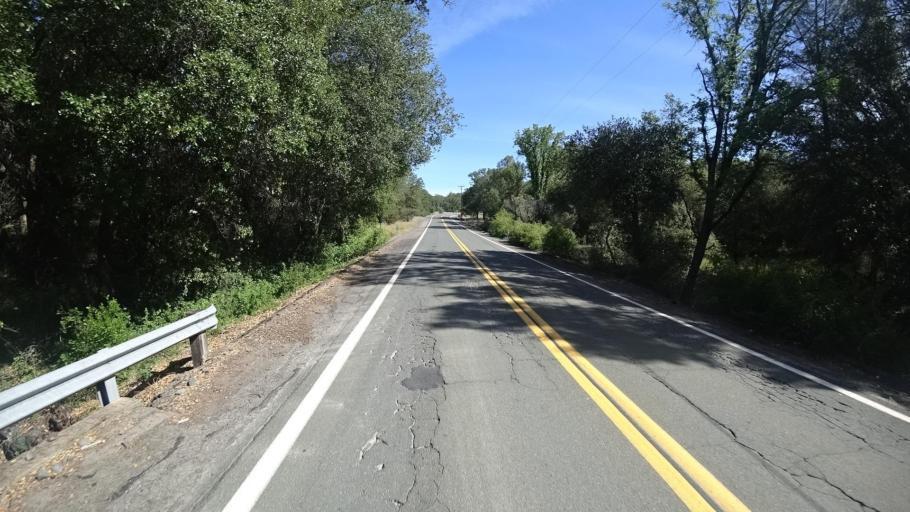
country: US
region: California
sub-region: Lake County
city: Kelseyville
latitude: 38.9425
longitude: -122.8154
